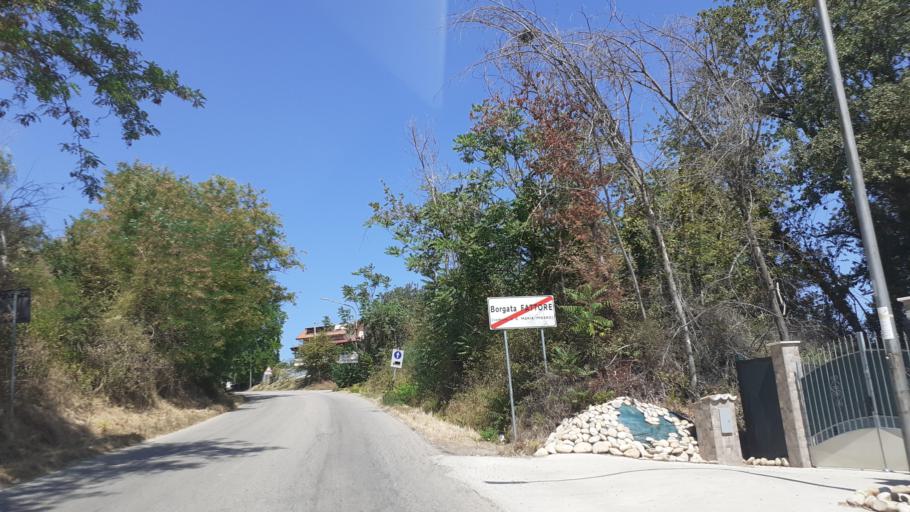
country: IT
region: Abruzzo
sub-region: Provincia di Chieti
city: Santa Maria Imbaro
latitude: 42.2156
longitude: 14.4539
